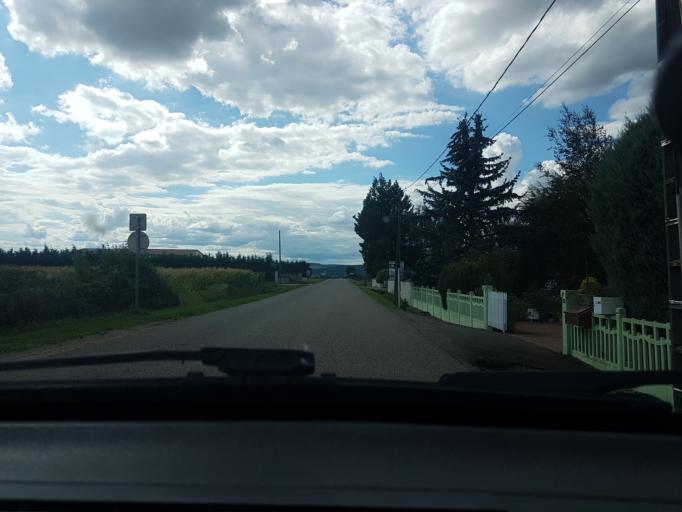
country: FR
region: Bourgogne
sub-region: Departement de Saone-et-Loire
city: Champforgeuil
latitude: 46.8429
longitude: 4.8097
